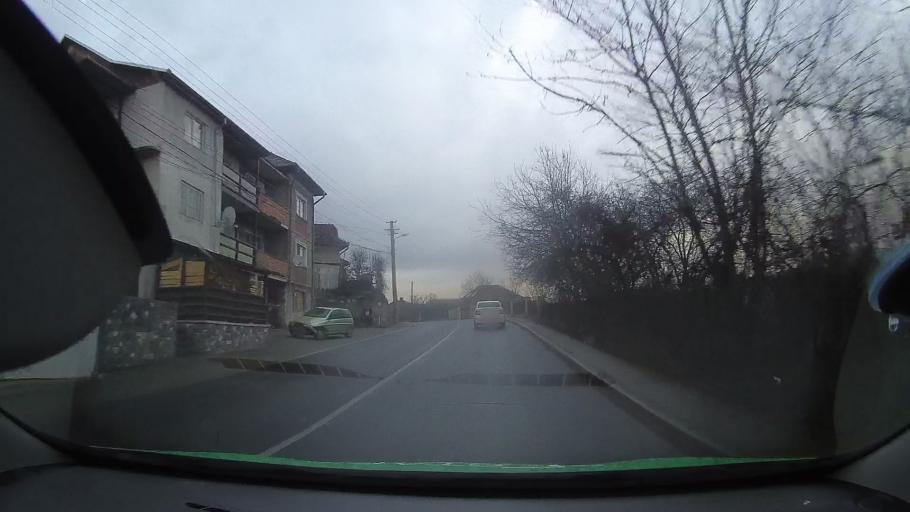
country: RO
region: Hunedoara
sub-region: Municipiul Brad
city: Brad
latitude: 46.1262
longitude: 22.7868
